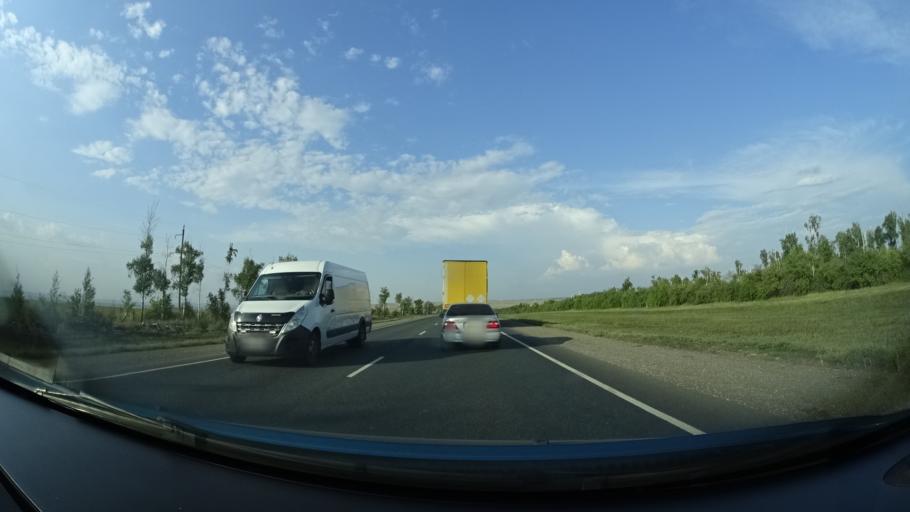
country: RU
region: Samara
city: Krasnyy Yar
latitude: 53.6735
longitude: 50.7698
